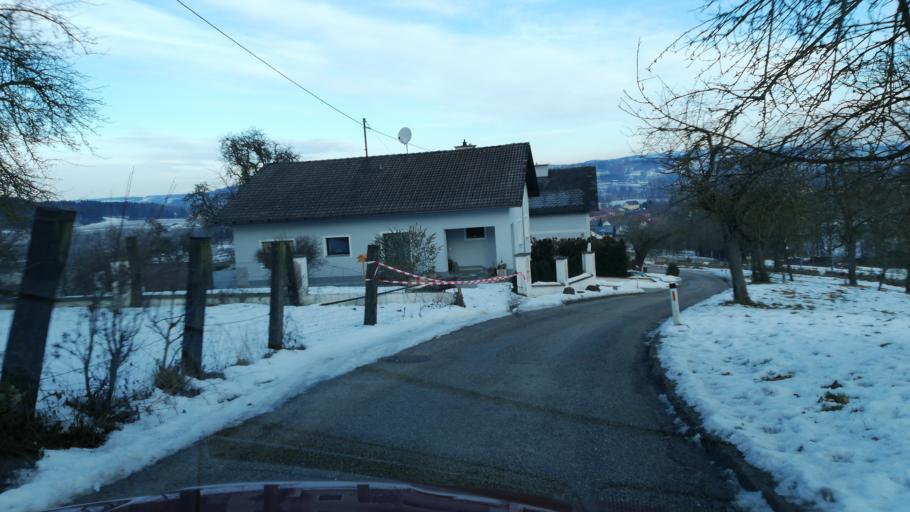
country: AT
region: Upper Austria
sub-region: Wels-Land
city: Buchkirchen
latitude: 48.2427
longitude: 13.9814
